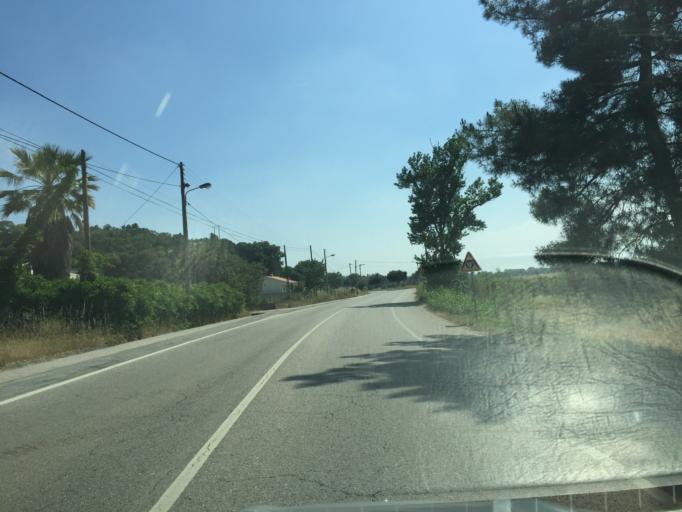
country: PT
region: Santarem
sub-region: Chamusca
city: Vila Nova da Barquinha
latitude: 39.4019
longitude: -8.4324
